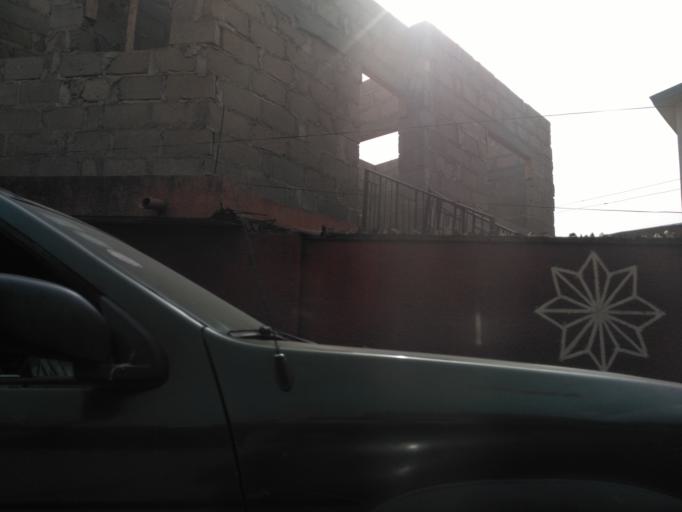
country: GH
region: Ashanti
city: Kumasi
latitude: 6.7032
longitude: -1.6042
